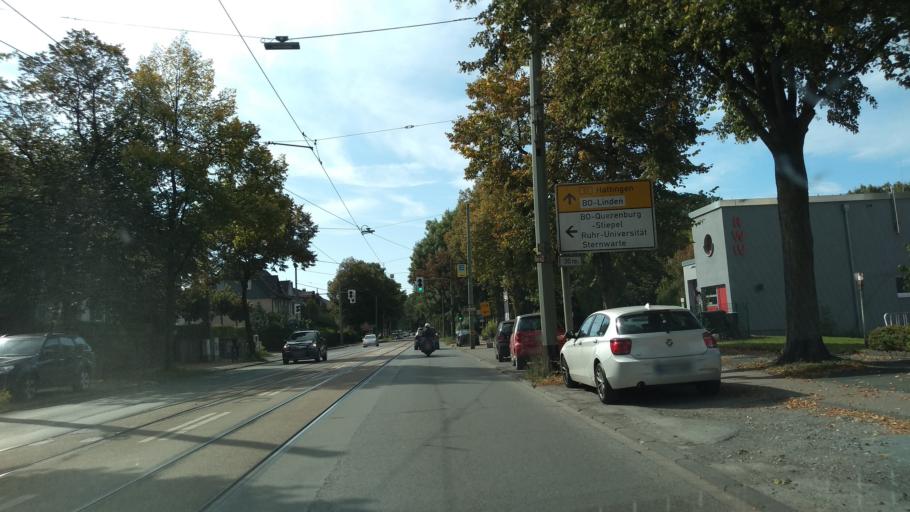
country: DE
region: North Rhine-Westphalia
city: Hattingen
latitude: 51.4425
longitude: 7.1921
